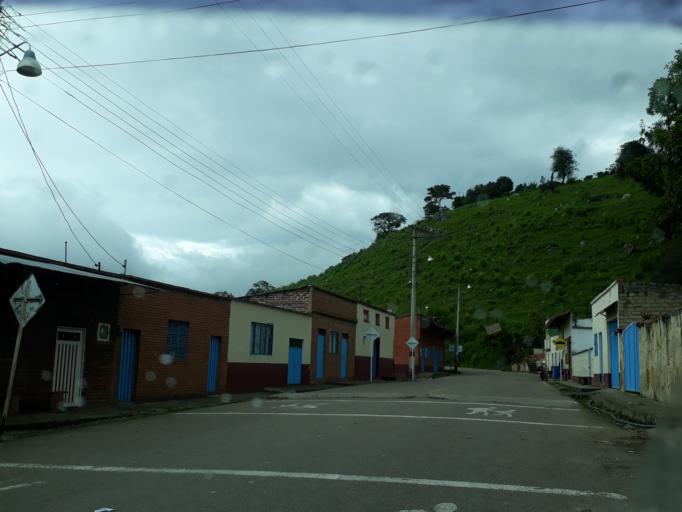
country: CO
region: Cundinamarca
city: Cabrera
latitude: 4.0258
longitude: -74.5137
